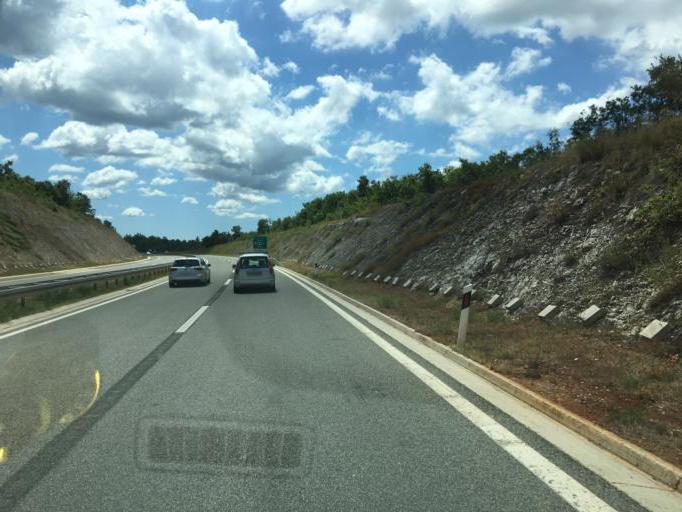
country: HR
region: Istarska
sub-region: Grad Porec
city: Porec
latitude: 45.2460
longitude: 13.7076
